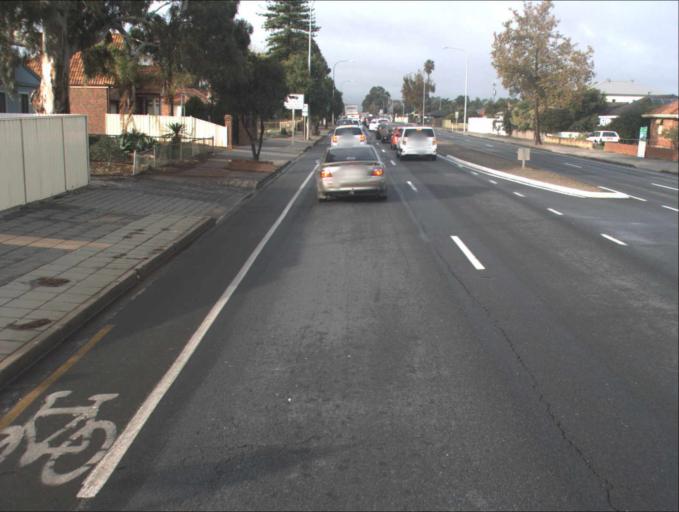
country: AU
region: South Australia
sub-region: Port Adelaide Enfield
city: Klemzig
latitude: -34.8687
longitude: 138.6189
